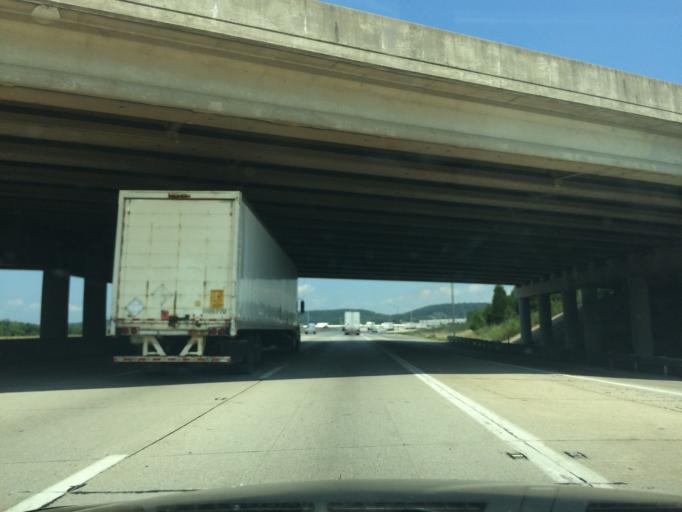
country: US
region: Kentucky
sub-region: Bullitt County
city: Shepherdsville
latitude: 37.9925
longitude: -85.7040
